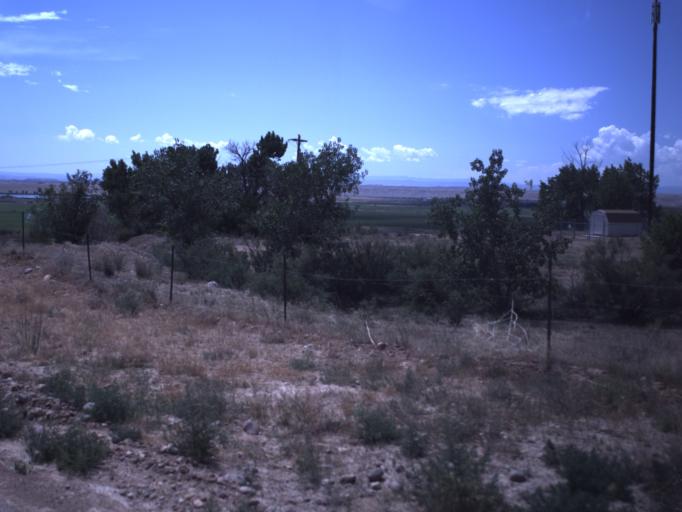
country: US
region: Utah
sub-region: Uintah County
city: Maeser
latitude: 40.2245
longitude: -109.6844
